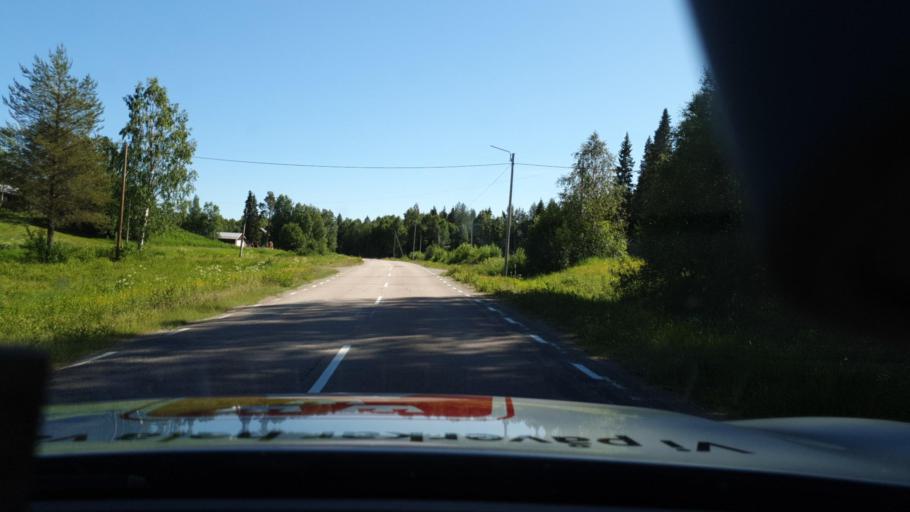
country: SE
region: Norrbotten
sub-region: Lulea Kommun
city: Ranea
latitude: 65.9440
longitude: 22.4006
